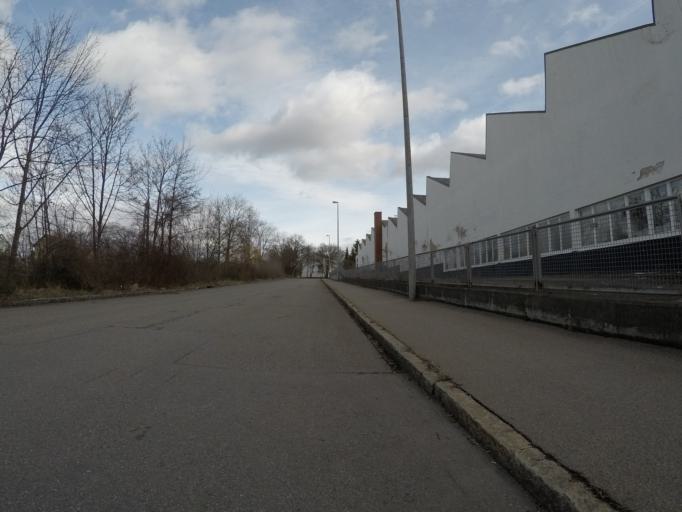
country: DE
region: Baden-Wuerttemberg
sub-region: Tuebingen Region
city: Reutlingen
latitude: 48.5057
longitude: 9.2161
